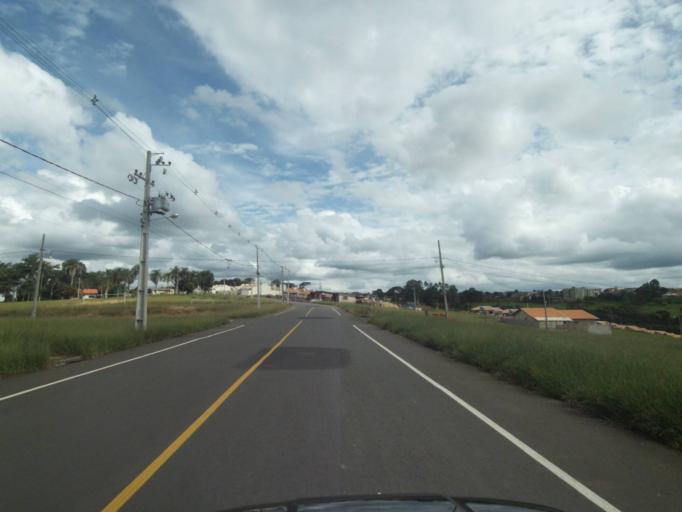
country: BR
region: Parana
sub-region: Telemaco Borba
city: Telemaco Borba
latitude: -24.3129
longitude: -50.6380
